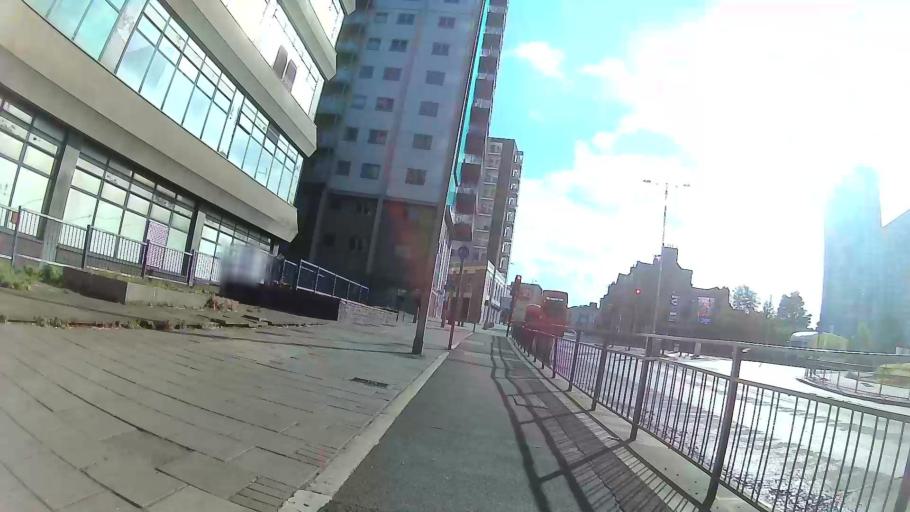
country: GB
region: England
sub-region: Greater London
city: Ilford
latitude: 51.5574
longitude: 0.0671
